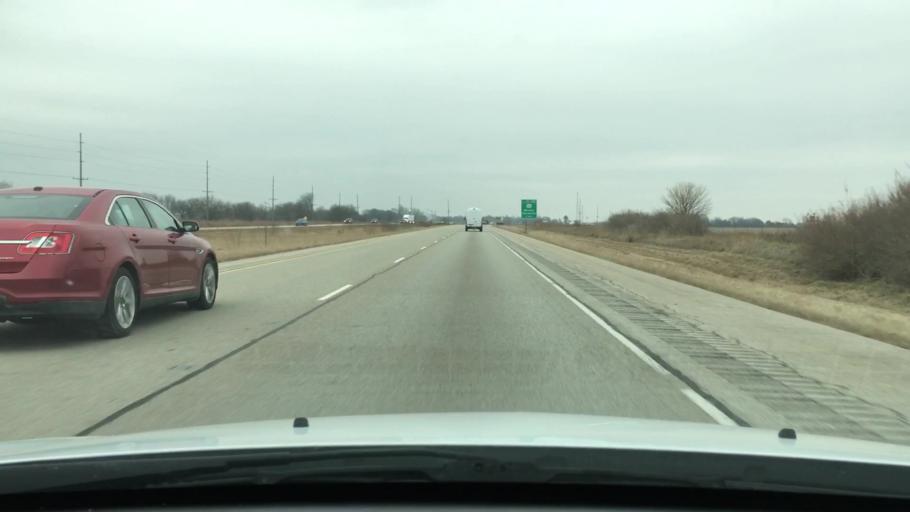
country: US
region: Illinois
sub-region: Logan County
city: Atlanta
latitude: 40.2986
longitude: -89.1869
